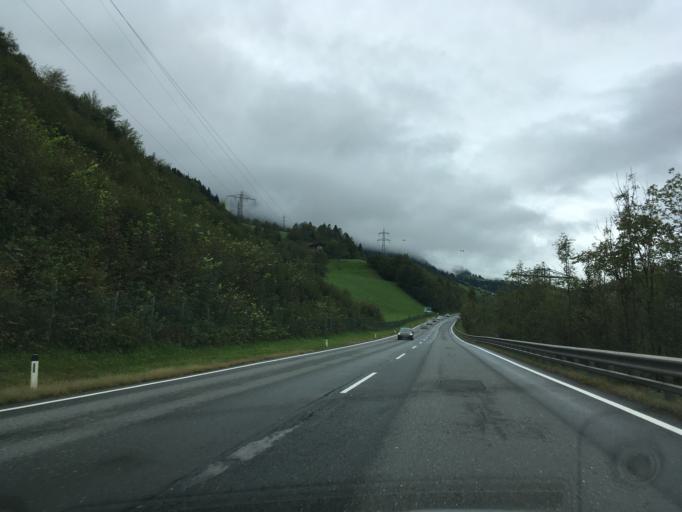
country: AT
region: Salzburg
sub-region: Politischer Bezirk Zell am See
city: Lend
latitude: 47.2972
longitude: 13.0757
